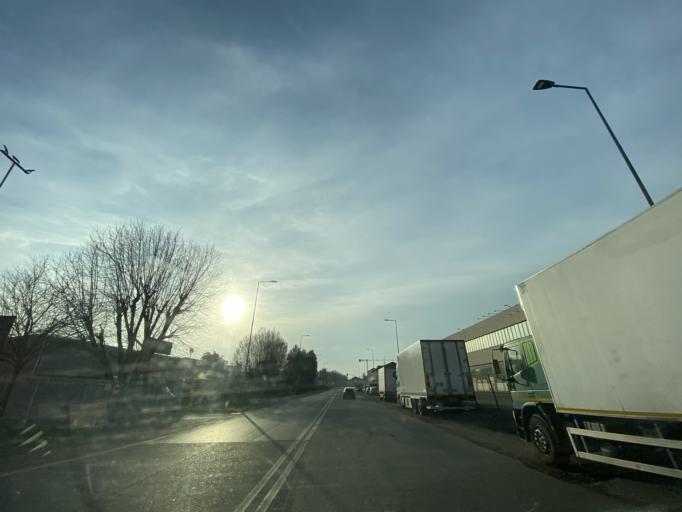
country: IT
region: Lombardy
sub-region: Citta metropolitana di Milano
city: Cassina de' Pecchi
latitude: 45.5165
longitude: 9.3472
